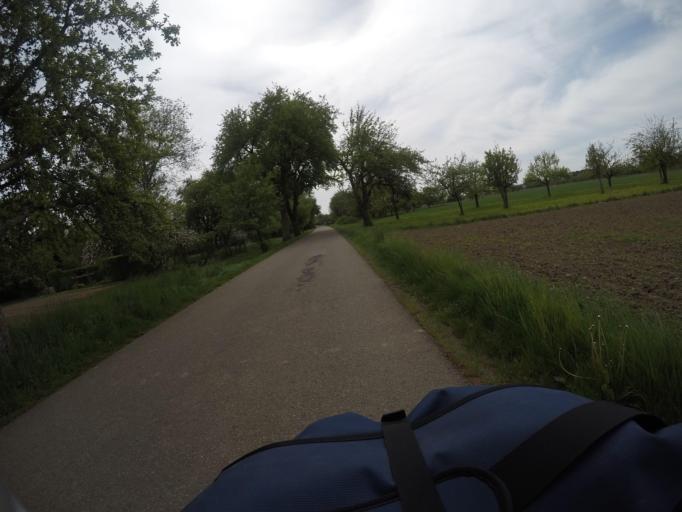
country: DE
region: Baden-Wuerttemberg
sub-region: Freiburg Region
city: Kehl
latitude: 48.5987
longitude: 7.8415
